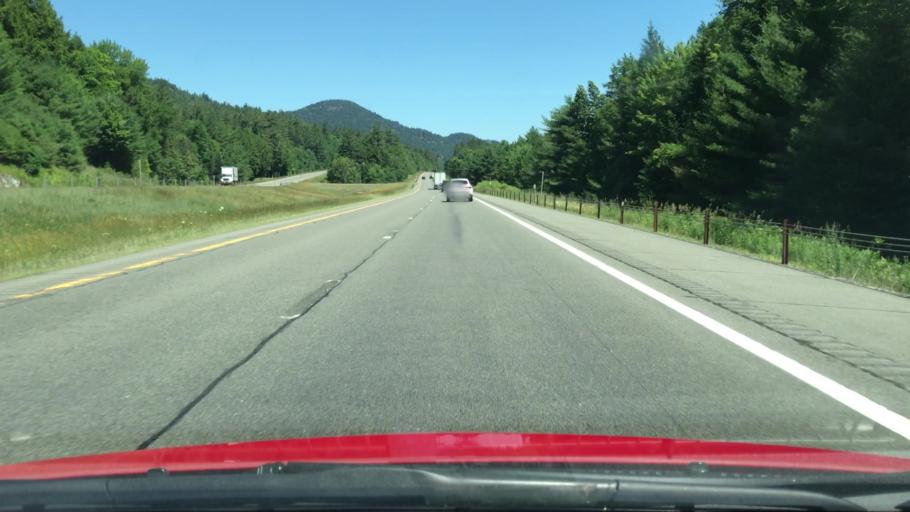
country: US
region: New York
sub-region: Essex County
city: Mineville
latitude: 43.9694
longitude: -73.7260
